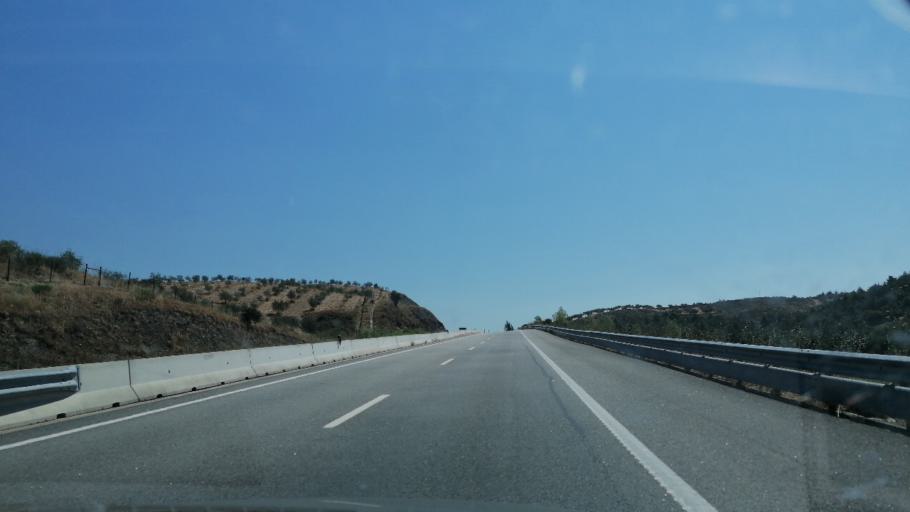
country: PT
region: Braganca
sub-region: Mirandela
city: Mirandela
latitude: 41.5188
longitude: -7.1391
